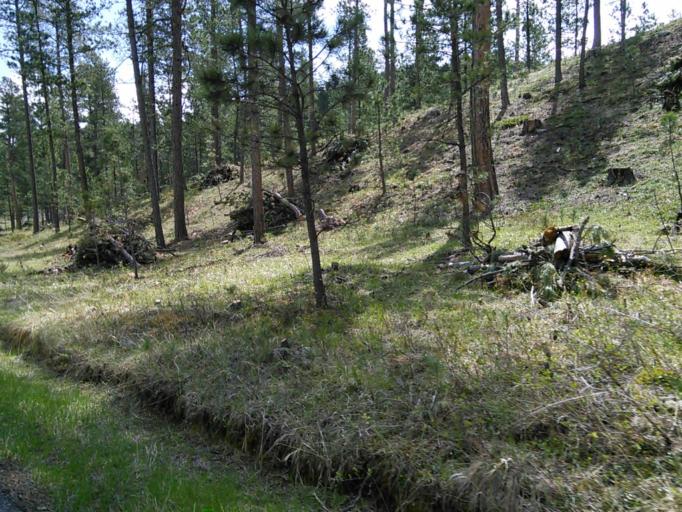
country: US
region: South Dakota
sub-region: Custer County
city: Custer
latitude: 43.7984
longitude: -103.4399
